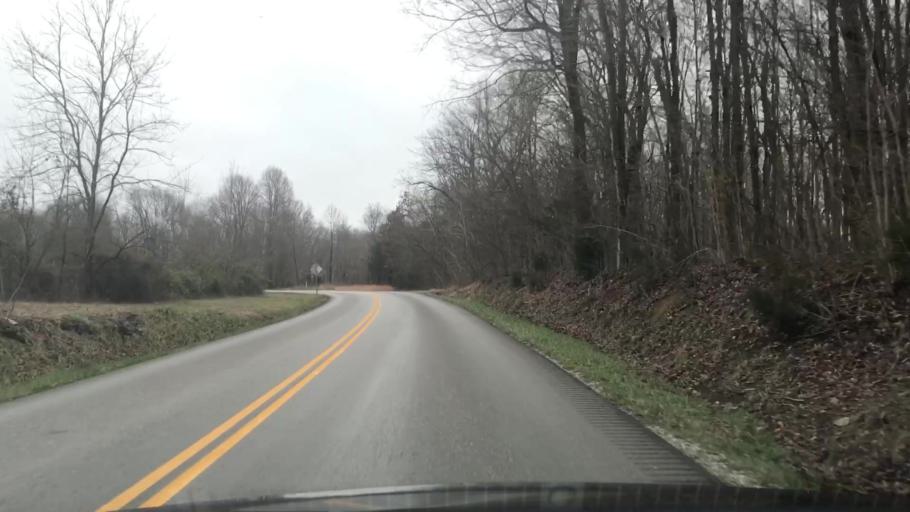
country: US
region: Kentucky
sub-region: Barren County
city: Glasgow
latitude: 36.8839
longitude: -85.7921
